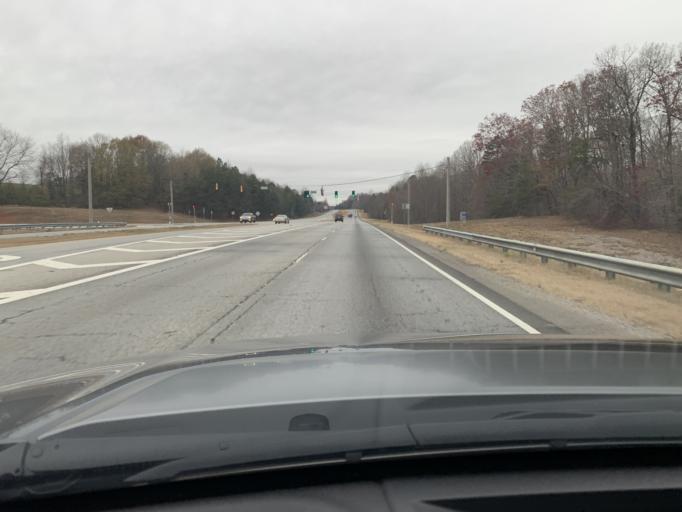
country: US
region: Georgia
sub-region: Habersham County
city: Mount Airy
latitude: 34.5645
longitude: -83.4941
